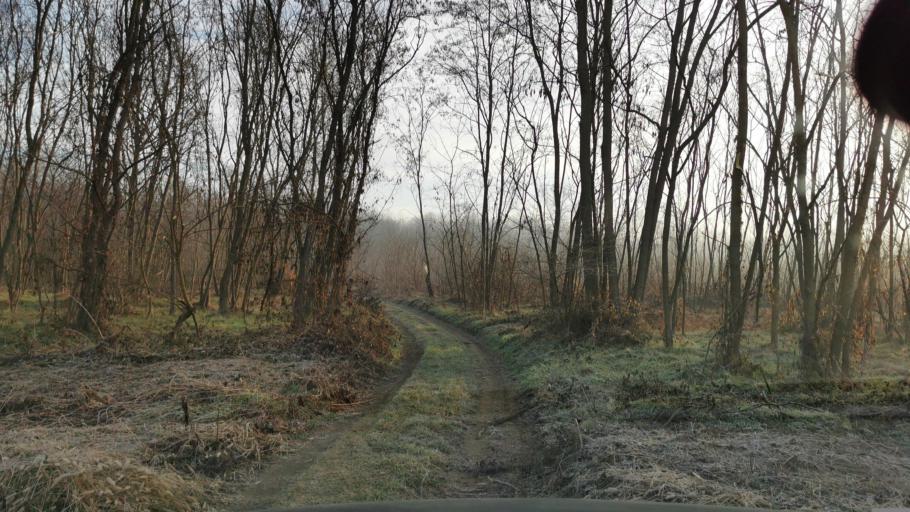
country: IT
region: Piedmont
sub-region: Provincia di Torino
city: Bosconero
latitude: 45.2709
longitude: 7.7905
